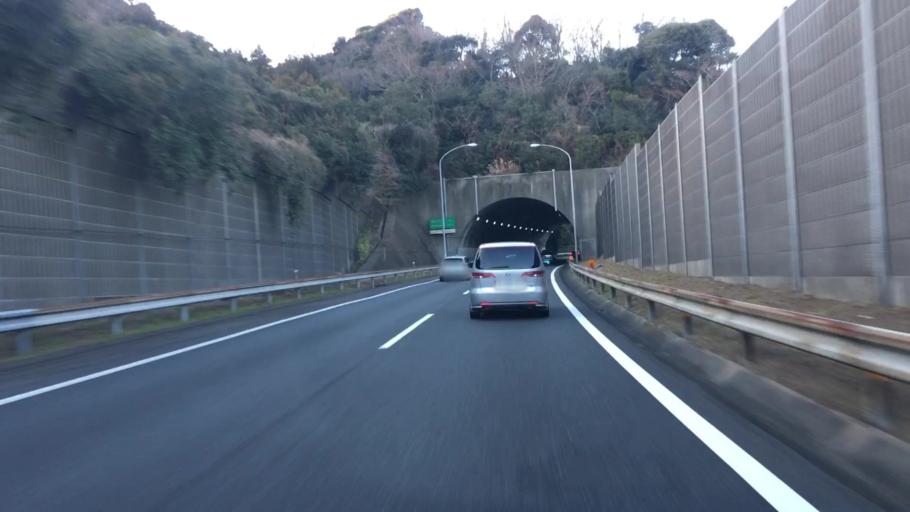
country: JP
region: Kanagawa
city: Zushi
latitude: 35.3266
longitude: 139.5967
